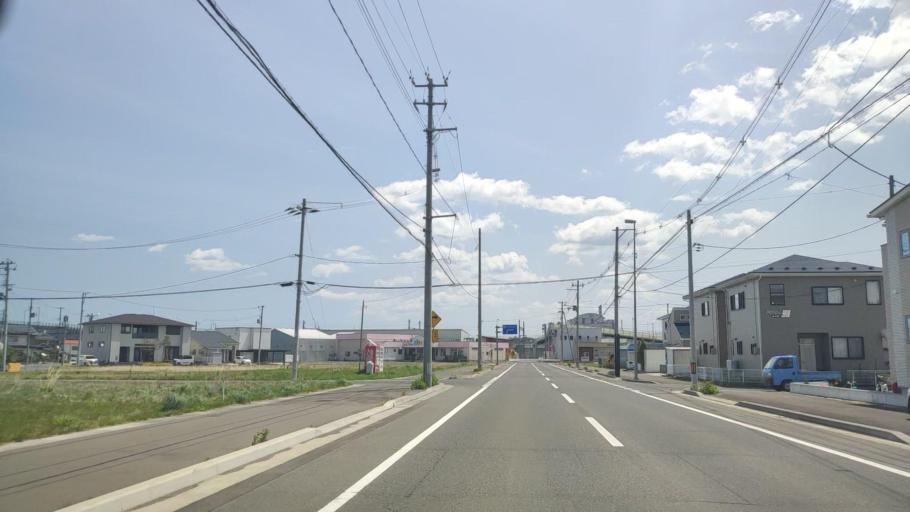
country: JP
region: Aomori
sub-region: Hachinohe Shi
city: Uchimaru
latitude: 40.5144
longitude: 141.4323
